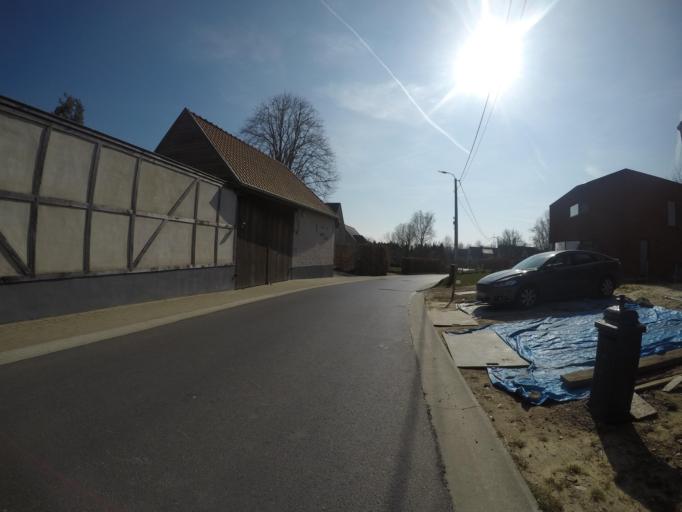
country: BE
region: Flanders
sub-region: Provincie Oost-Vlaanderen
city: Sint-Maria-Lierde
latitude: 50.7825
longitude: 3.8387
